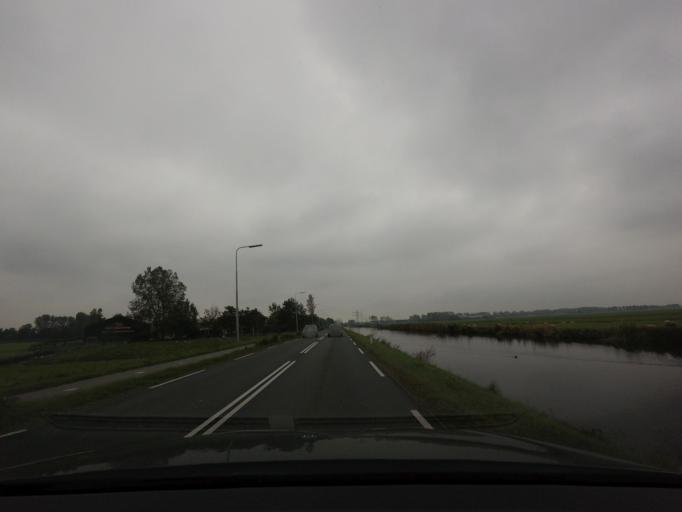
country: NL
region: South Holland
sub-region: Gemeente Teylingen
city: Voorhout
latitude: 52.2099
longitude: 4.4804
